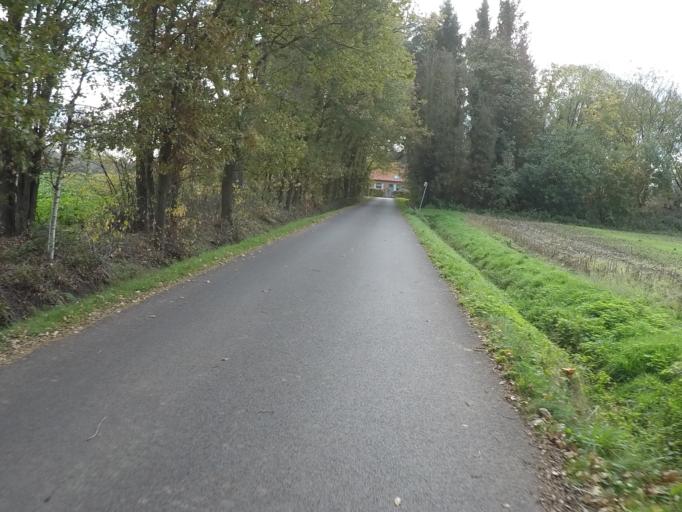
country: BE
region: Flanders
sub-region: Provincie Antwerpen
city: Berlaar
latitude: 51.1405
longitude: 4.6536
